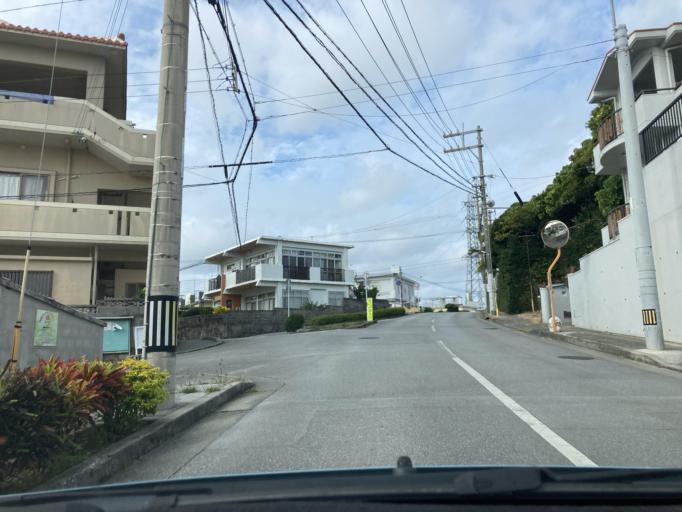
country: JP
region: Okinawa
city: Ginowan
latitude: 26.2037
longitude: 127.7502
